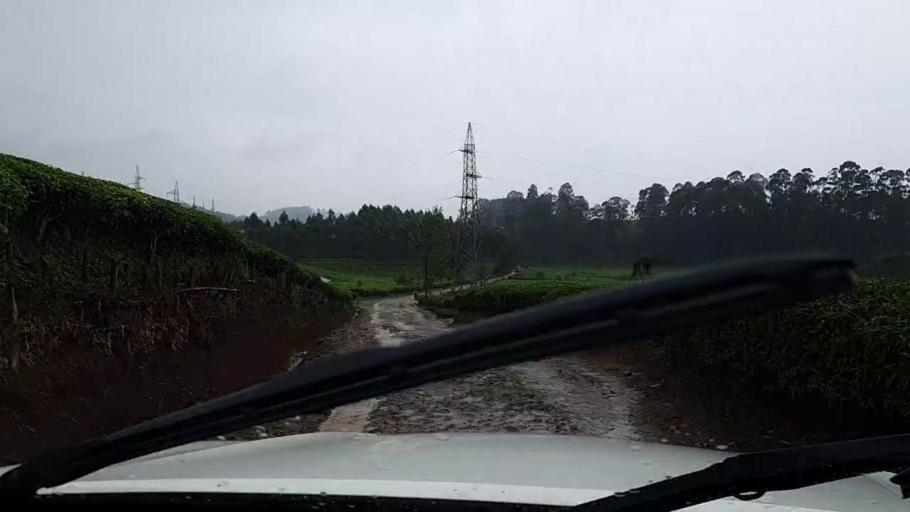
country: RW
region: Western Province
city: Cyangugu
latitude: -2.4530
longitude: 29.0400
